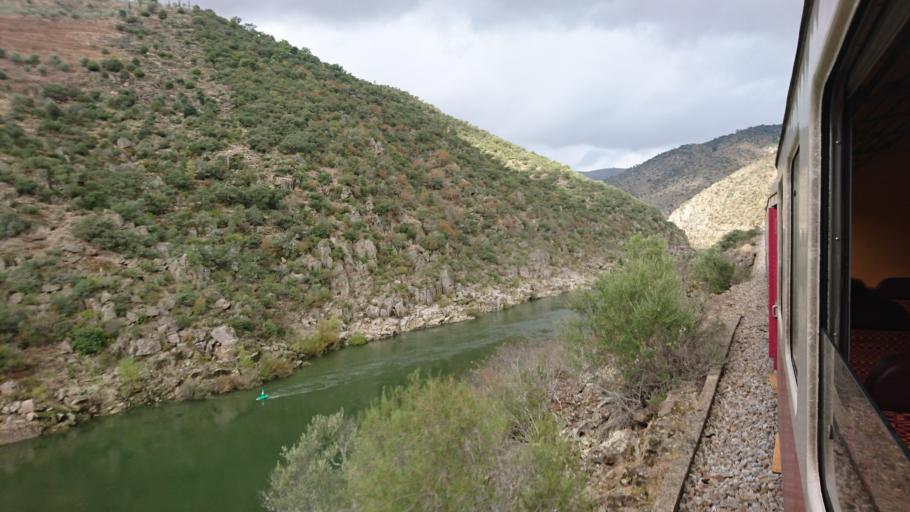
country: PT
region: Viseu
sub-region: Sao Joao da Pesqueira
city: Sao Joao da Pesqueira
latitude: 41.1860
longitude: -7.3860
